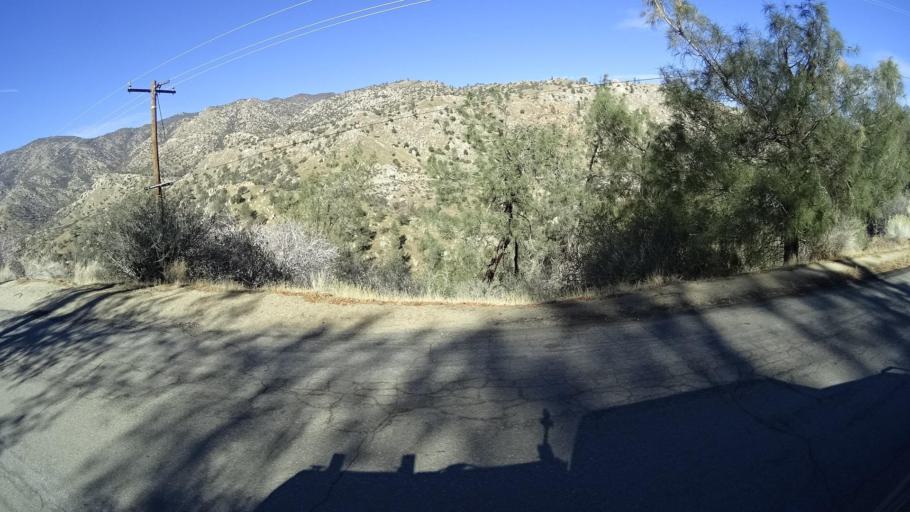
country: US
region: California
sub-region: Kern County
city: Bodfish
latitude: 35.5753
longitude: -118.5444
